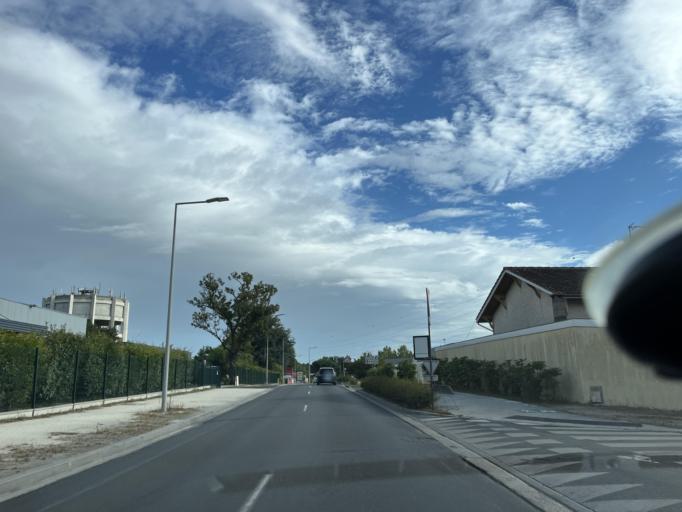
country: FR
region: Aquitaine
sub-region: Departement de la Gironde
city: Le Haillan
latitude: 44.8670
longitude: -0.6638
